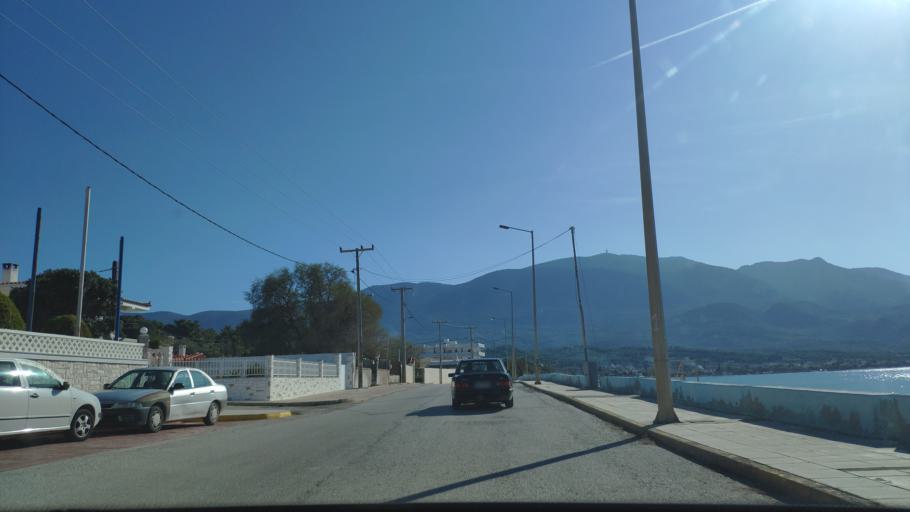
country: GR
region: Attica
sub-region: Nomarchia Dytikis Attikis
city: Kineta
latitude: 38.0826
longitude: 23.1771
